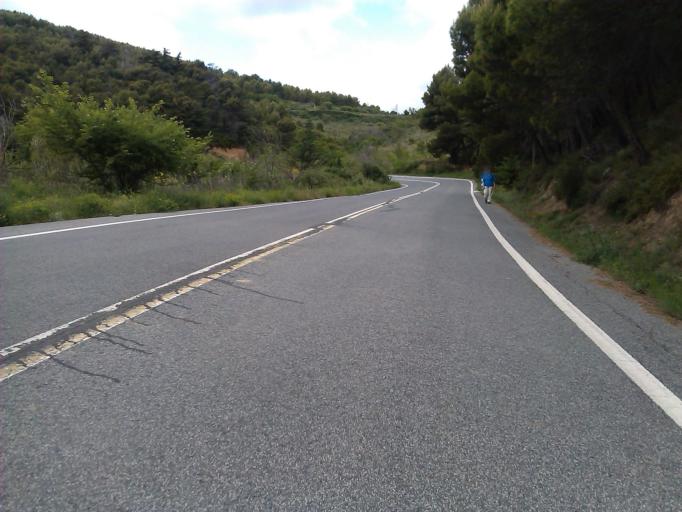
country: ES
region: Navarre
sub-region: Provincia de Navarra
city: Maneru
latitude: 42.6683
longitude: -1.8450
